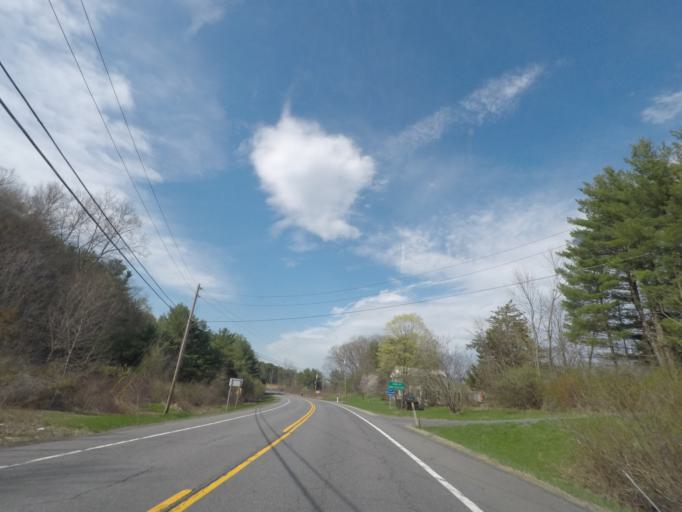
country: US
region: New York
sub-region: Albany County
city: Voorheesville
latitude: 42.5386
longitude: -73.9419
